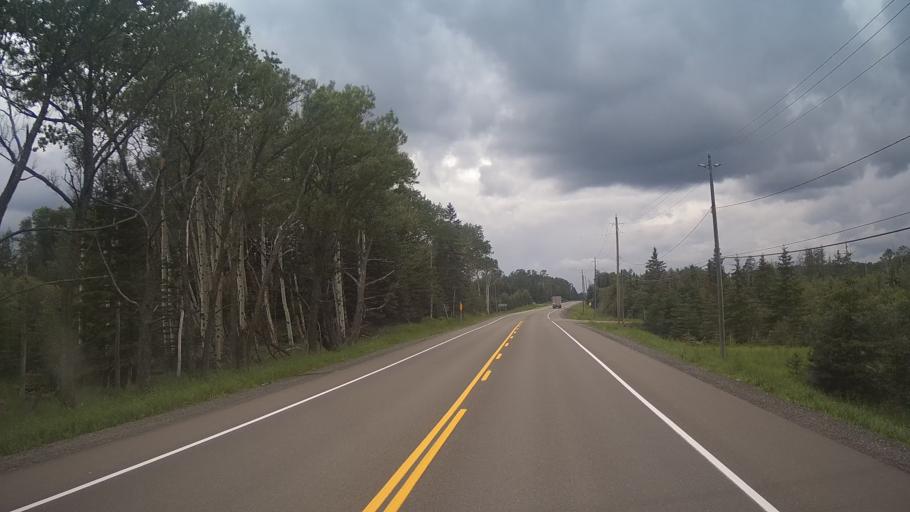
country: CA
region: Ontario
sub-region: Thunder Bay District
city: Thunder Bay
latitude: 48.4884
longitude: -89.3485
